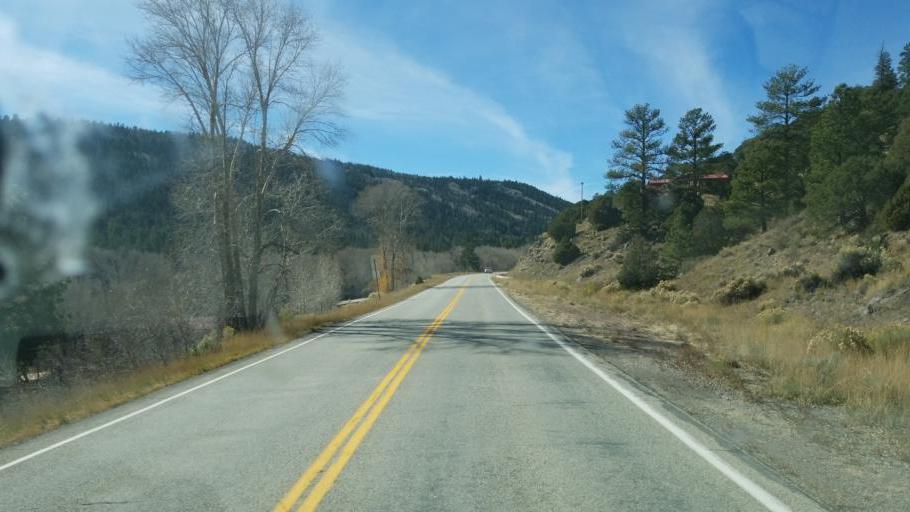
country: US
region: Colorado
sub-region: Conejos County
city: Conejos
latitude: 37.0687
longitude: -106.2458
